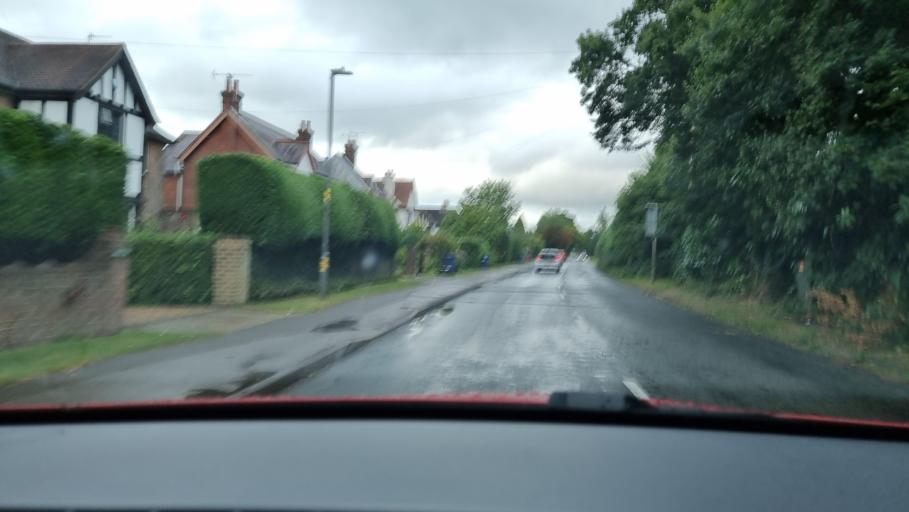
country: GB
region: England
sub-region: Buckinghamshire
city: Chesham
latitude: 51.7101
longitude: -0.5991
